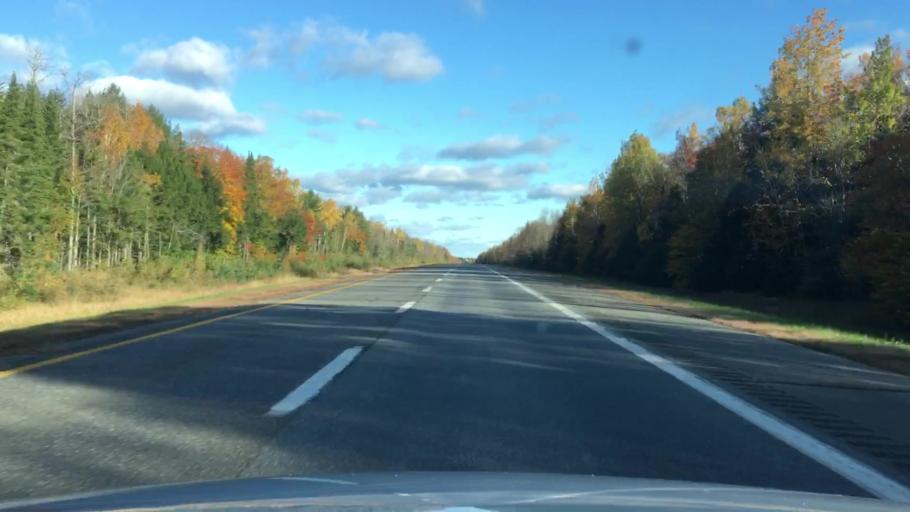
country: US
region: Maine
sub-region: Penobscot County
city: Greenbush
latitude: 45.0778
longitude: -68.6916
